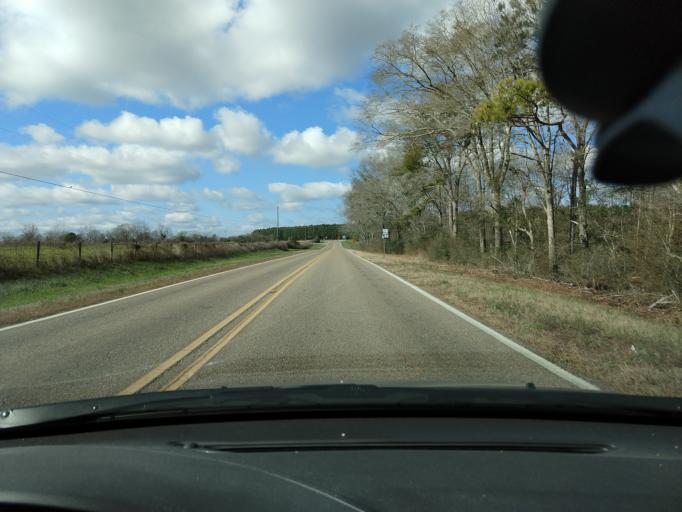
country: US
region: Alabama
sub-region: Coffee County
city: Elba
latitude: 31.3114
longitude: -86.0290
